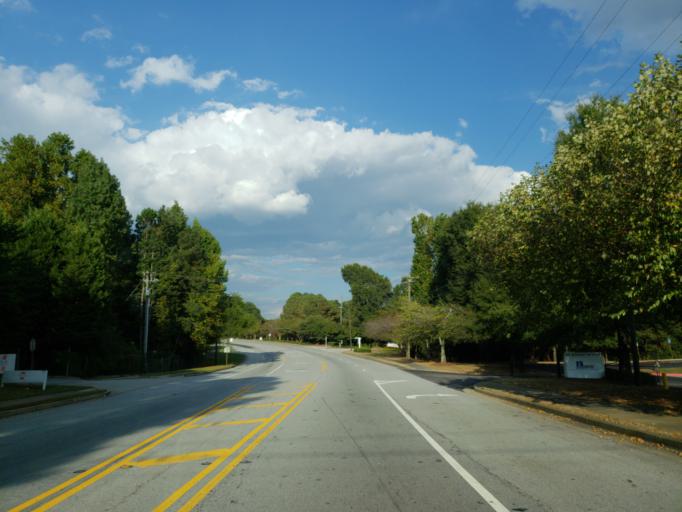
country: US
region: Georgia
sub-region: Cobb County
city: Mableton
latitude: 33.7546
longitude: -84.5722
